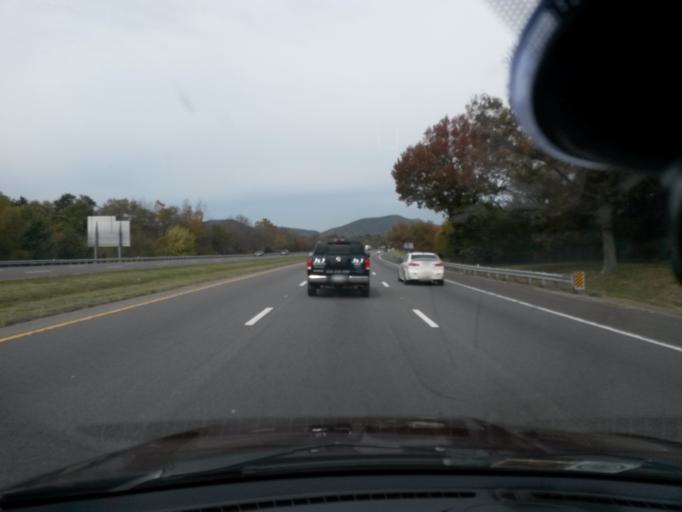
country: US
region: Virginia
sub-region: Roanoke County
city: Hollins
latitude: 37.3158
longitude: -79.9810
